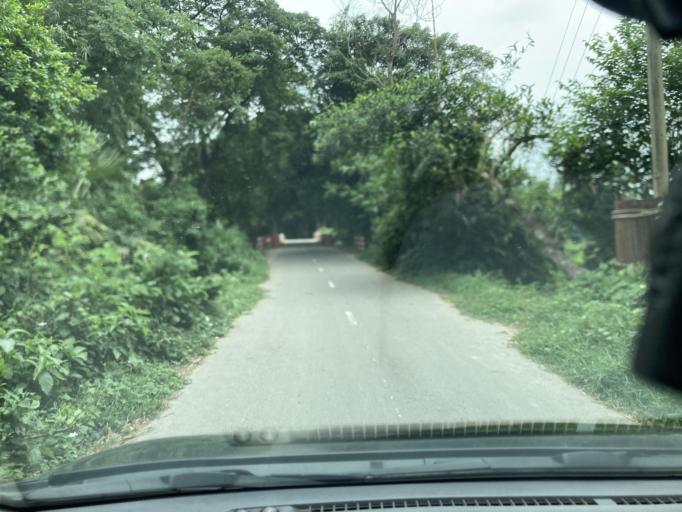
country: BD
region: Dhaka
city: Dohar
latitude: 23.7784
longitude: 90.0663
